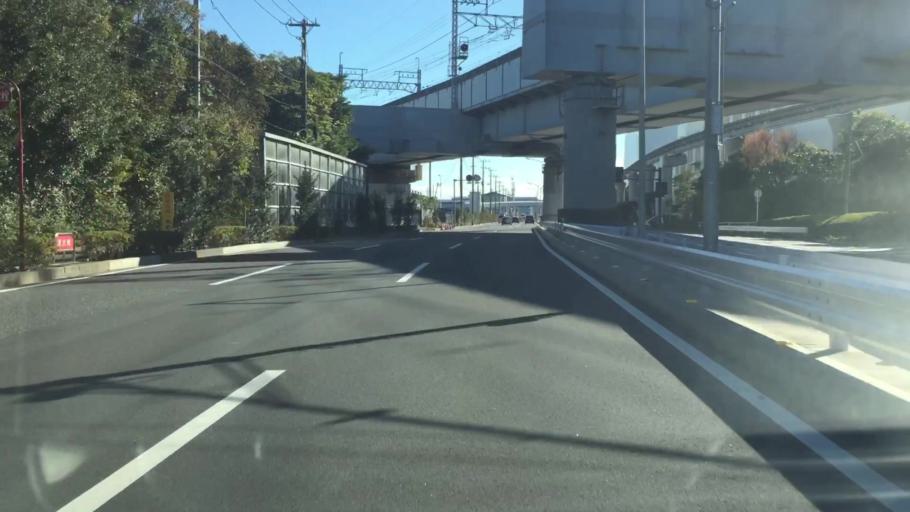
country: JP
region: Tokyo
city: Urayasu
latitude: 35.6353
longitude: 139.8870
